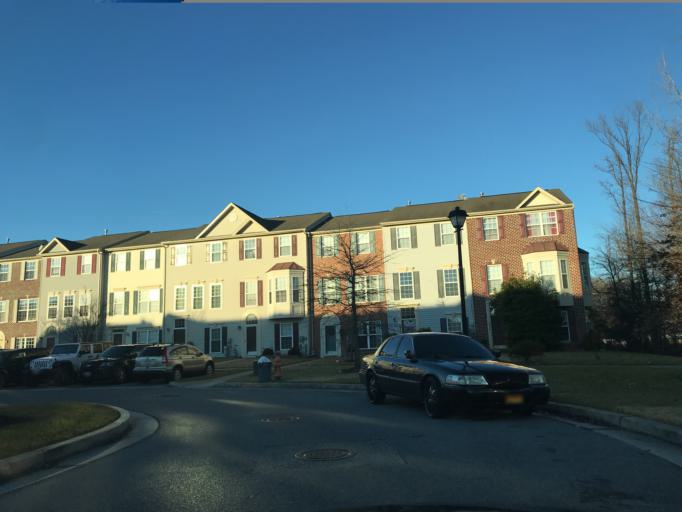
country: US
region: Maryland
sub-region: Baltimore County
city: Bowleys Quarters
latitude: 39.3293
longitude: -76.3818
